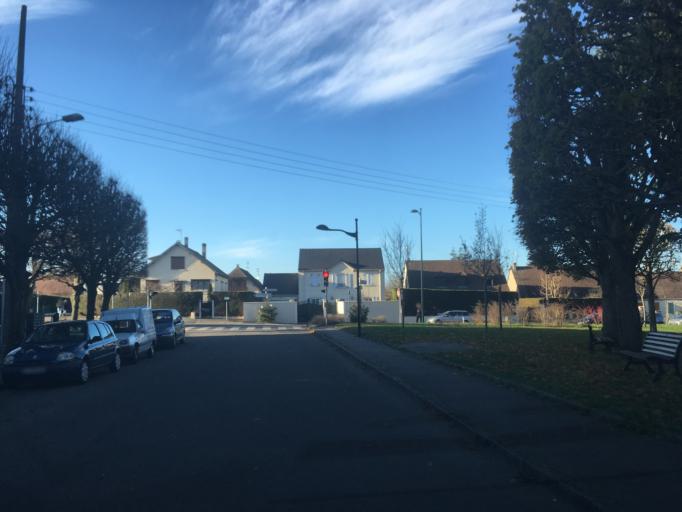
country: FR
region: Haute-Normandie
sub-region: Departement de l'Eure
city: Vernon
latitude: 49.0839
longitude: 1.4872
